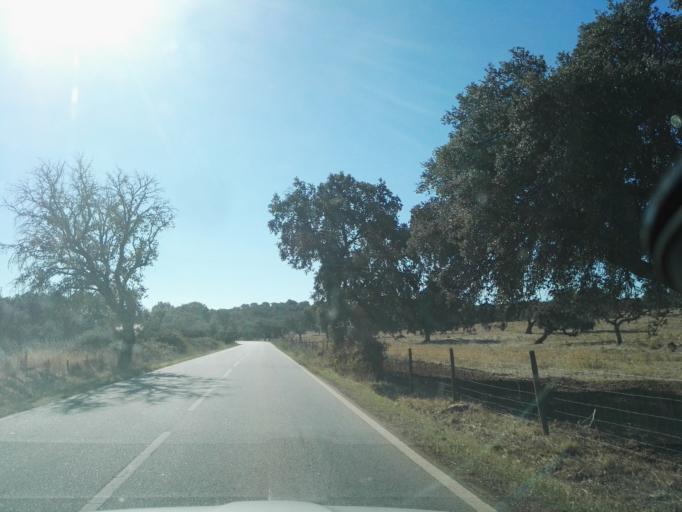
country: PT
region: Portalegre
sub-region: Elvas
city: Elvas
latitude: 38.9141
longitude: -7.1820
